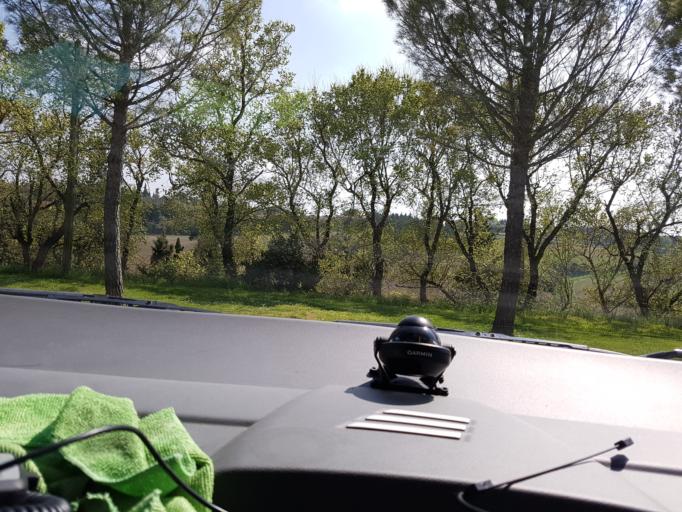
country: FR
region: Languedoc-Roussillon
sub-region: Departement de l'Aude
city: Bram
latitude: 43.1861
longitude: 2.0324
